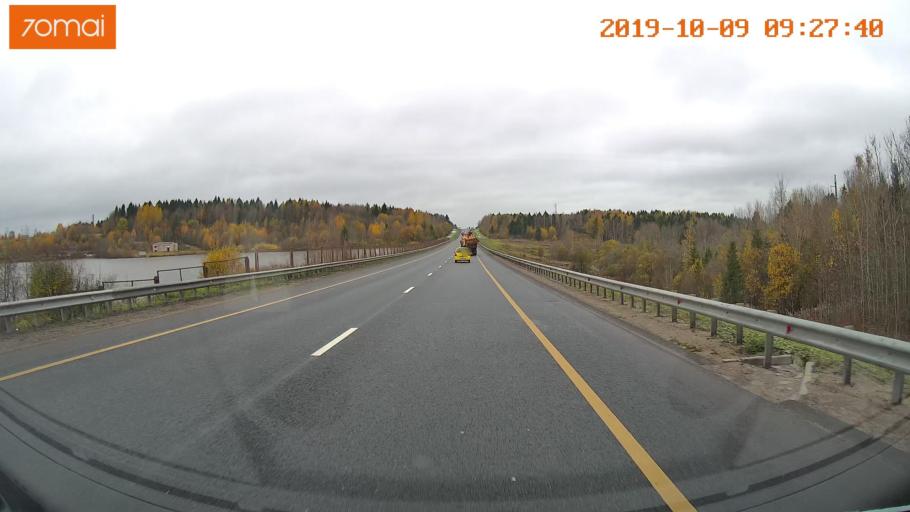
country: RU
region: Vologda
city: Vologda
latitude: 59.1153
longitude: 39.9759
